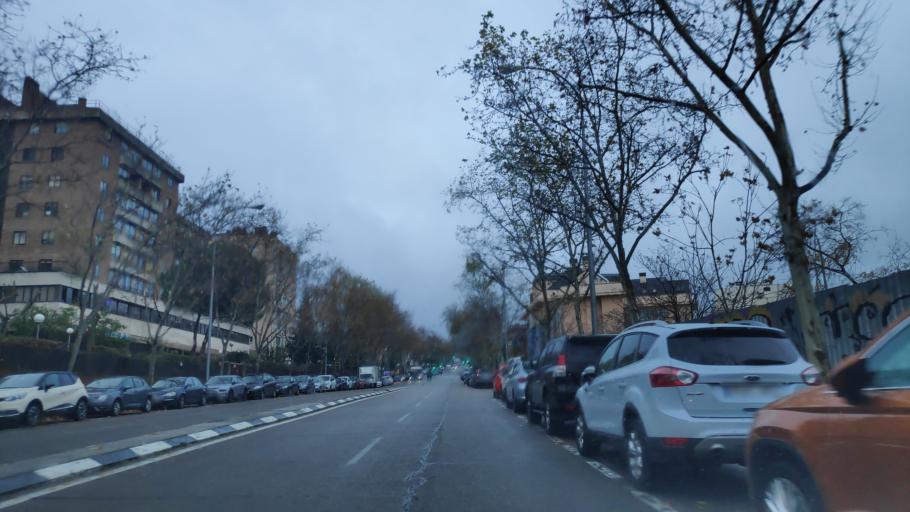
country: ES
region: Madrid
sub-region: Provincia de Madrid
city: Ciudad Lineal
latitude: 40.4573
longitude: -3.6456
